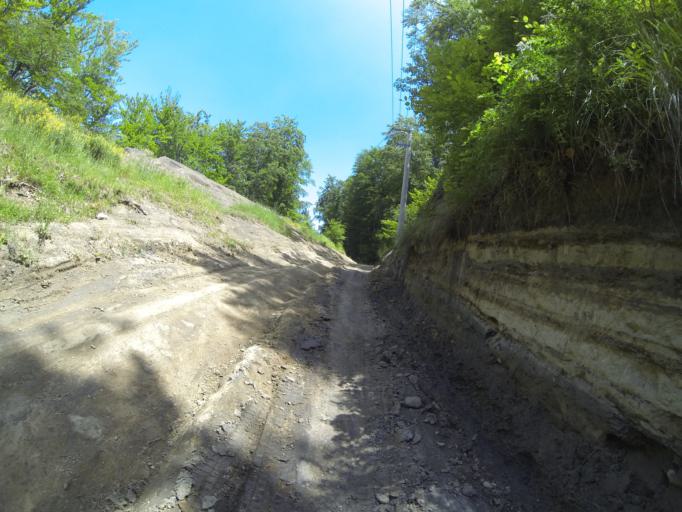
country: RO
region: Valcea
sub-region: Oras Baile Olanesti
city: Baile Olanesti
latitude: 45.2100
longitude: 24.2064
